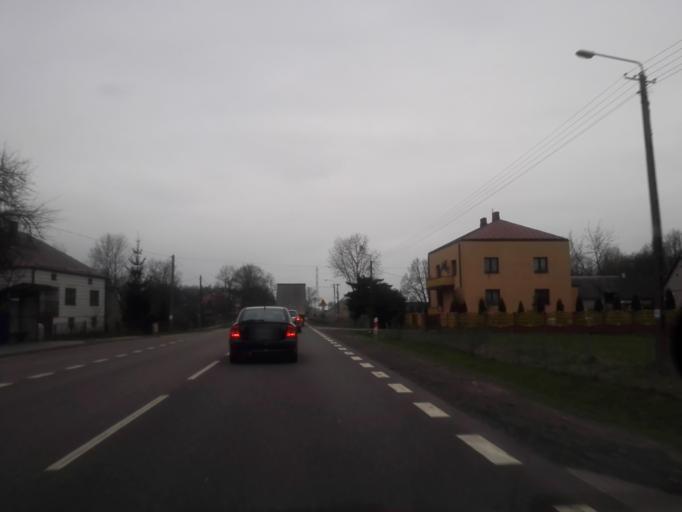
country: PL
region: Podlasie
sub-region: Powiat grajewski
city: Szczuczyn
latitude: 53.5937
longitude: 22.3451
